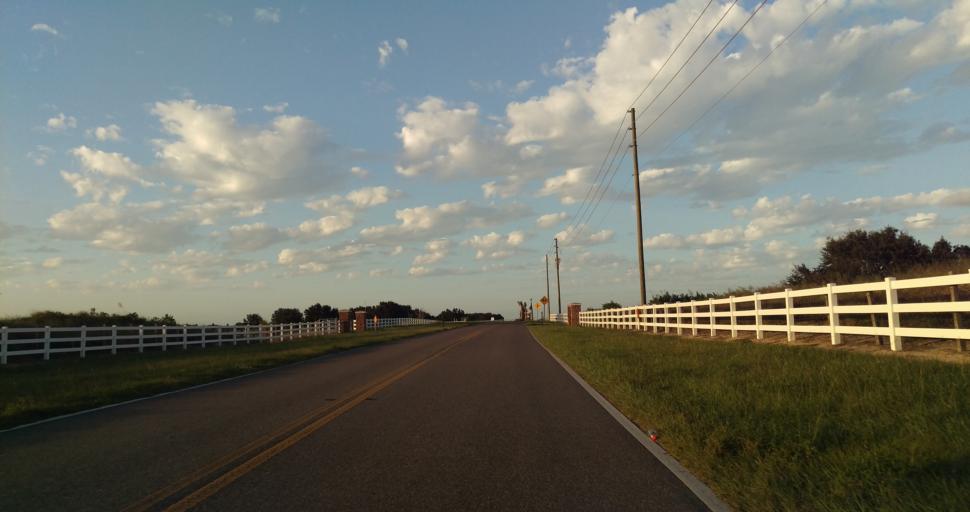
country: US
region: Florida
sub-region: Orange County
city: Lake Butler
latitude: 28.4437
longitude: -81.6237
